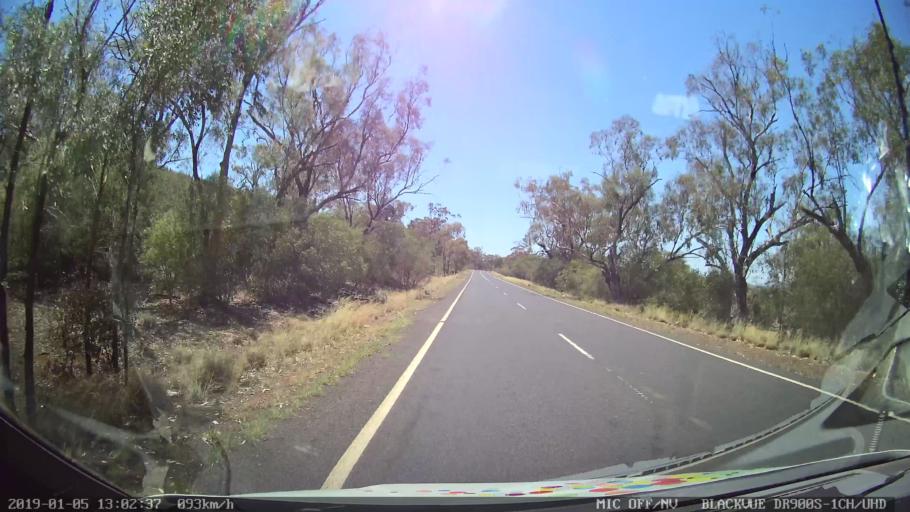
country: AU
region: New South Wales
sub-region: Gunnedah
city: Gunnedah
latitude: -31.1140
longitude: 149.8144
